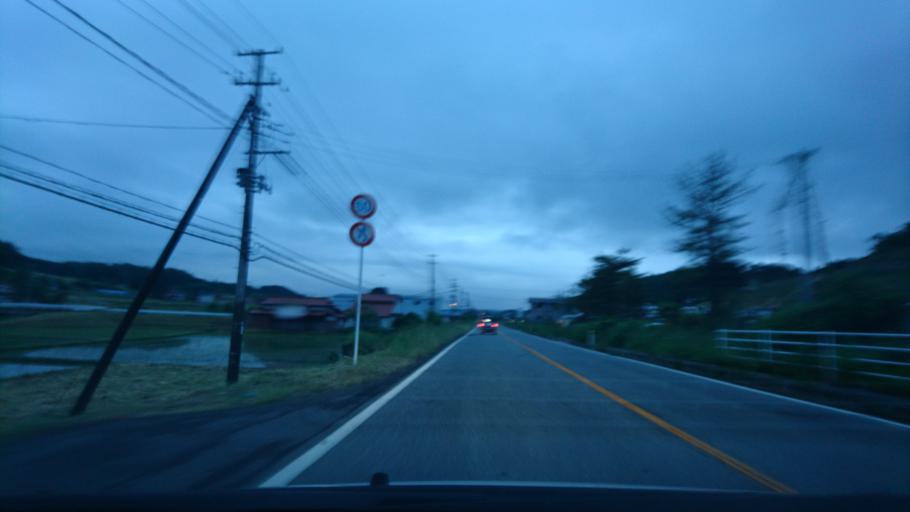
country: JP
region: Iwate
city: Ichinoseki
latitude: 38.8264
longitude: 141.0805
